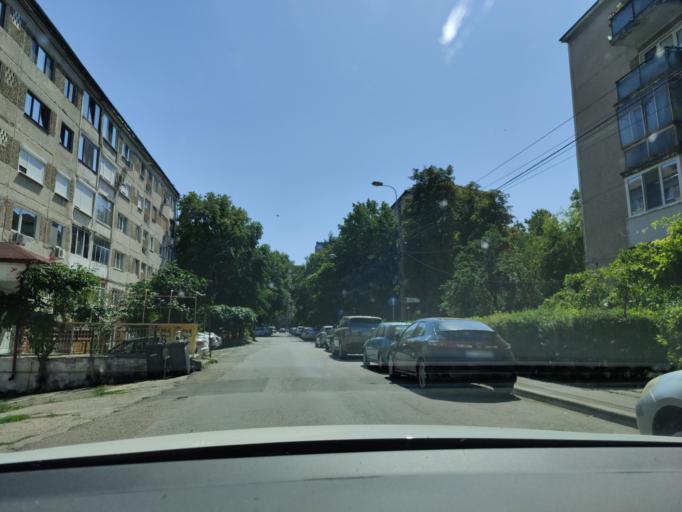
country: RO
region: Timis
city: Timisoara
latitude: 45.7636
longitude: 21.2150
